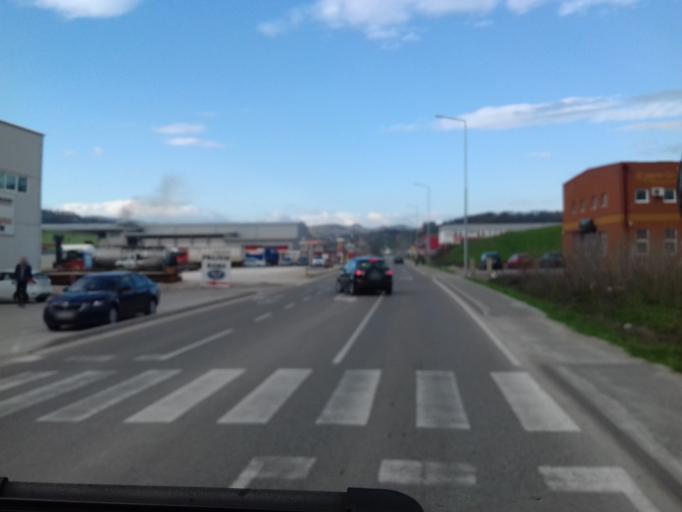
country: BA
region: Federation of Bosnia and Herzegovina
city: Tesanj
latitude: 44.6332
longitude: 18.0067
